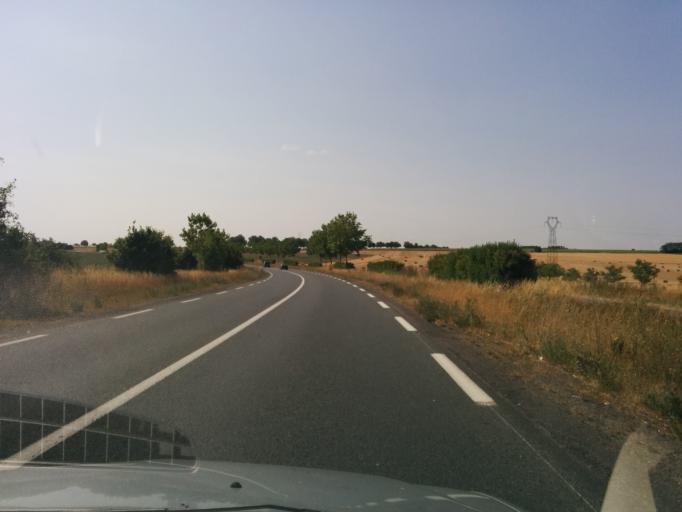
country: FR
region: Poitou-Charentes
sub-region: Departement de la Vienne
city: Neuville-de-Poitou
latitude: 46.7121
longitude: 0.2253
